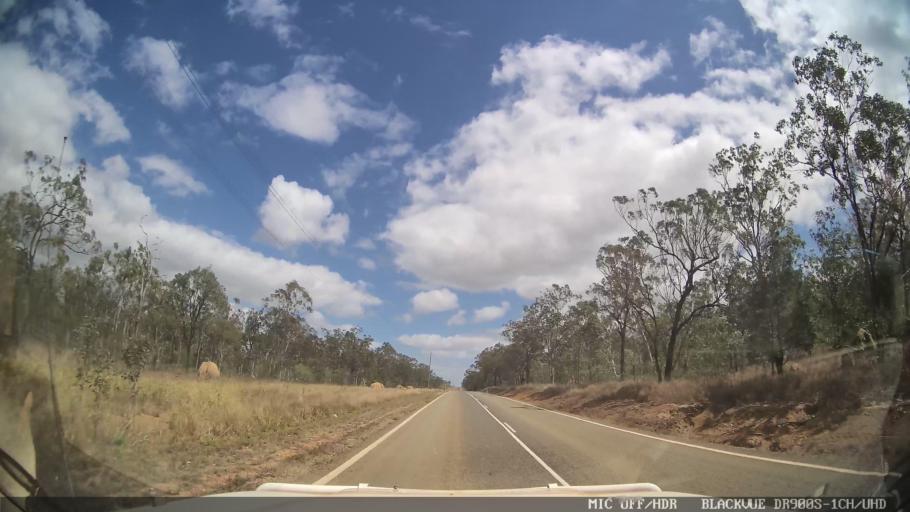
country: AU
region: Queensland
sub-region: Tablelands
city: Ravenshoe
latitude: -17.7245
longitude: 145.0503
